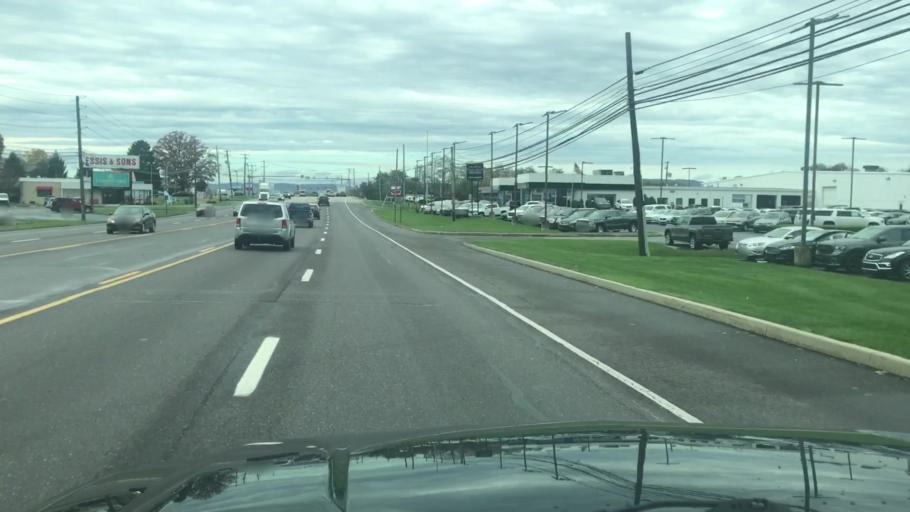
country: US
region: Pennsylvania
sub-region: Cumberland County
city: Mechanicsburg
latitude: 40.2444
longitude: -76.9951
